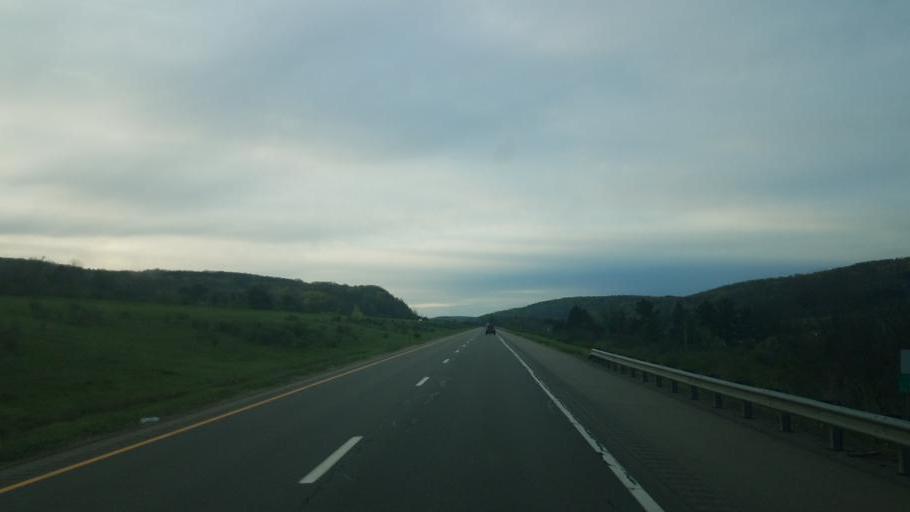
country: US
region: New York
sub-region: Allegany County
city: Cuba
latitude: 42.2235
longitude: -78.2427
